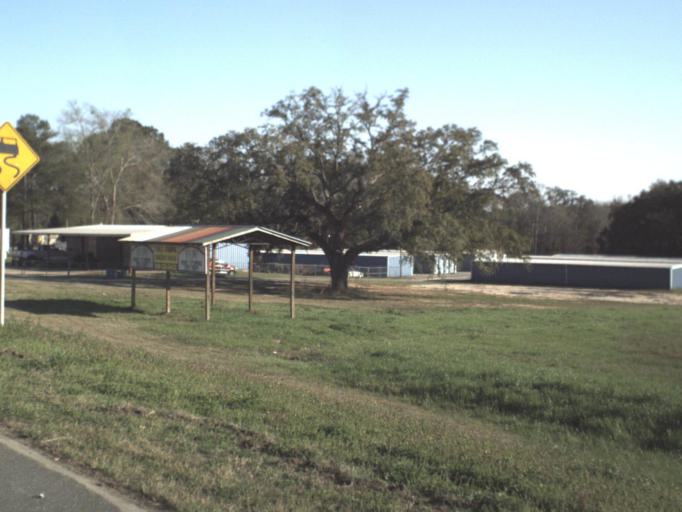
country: US
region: Florida
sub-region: Jackson County
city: Sneads
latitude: 30.7106
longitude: -84.9403
